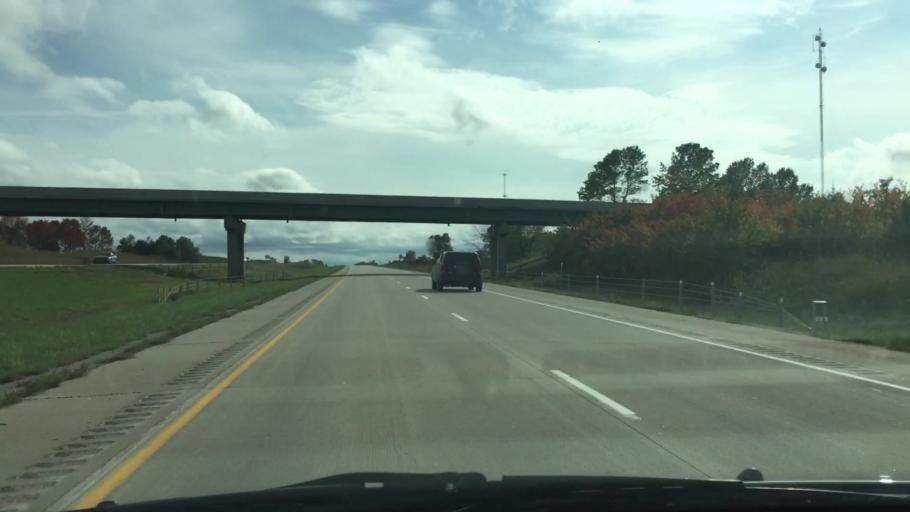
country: US
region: Iowa
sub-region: Decatur County
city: Leon
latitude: 40.8708
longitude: -93.8026
